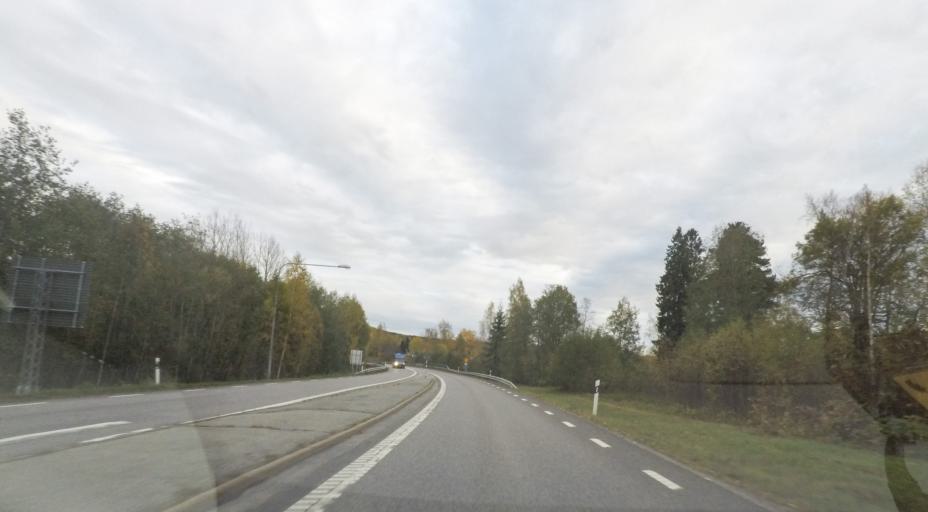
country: SE
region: OErebro
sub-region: Nora Kommun
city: As
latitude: 59.5083
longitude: 14.9659
